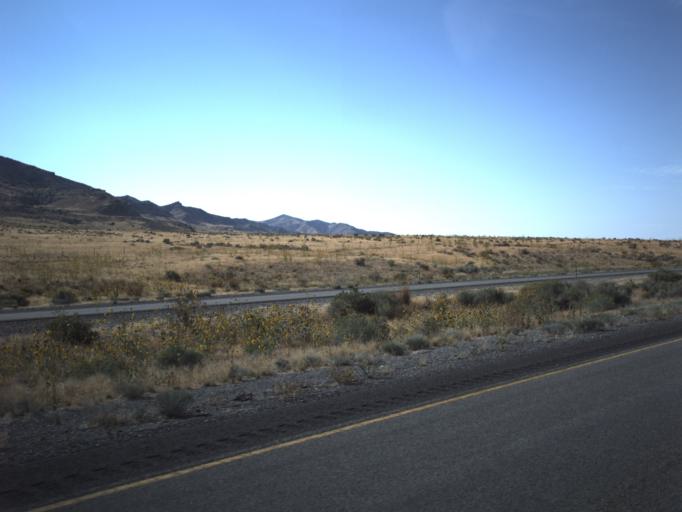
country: US
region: Utah
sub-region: Tooele County
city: Grantsville
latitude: 40.8061
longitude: -112.9359
